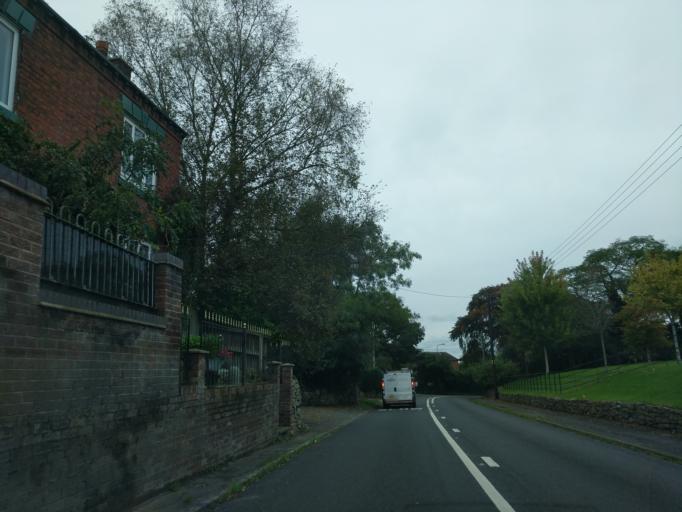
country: GB
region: England
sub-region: Cheshire East
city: Chorlton
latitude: 53.0199
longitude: -2.3692
